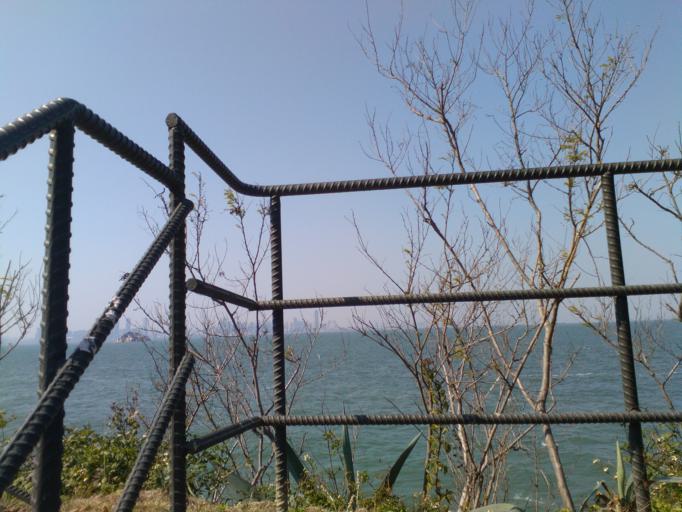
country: TW
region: Fukien
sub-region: Kinmen
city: Jincheng
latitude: 24.4494
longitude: 118.2381
